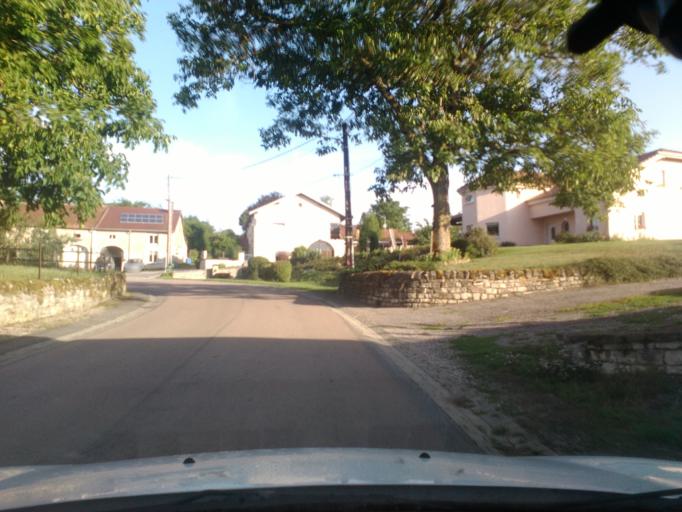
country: FR
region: Lorraine
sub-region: Departement des Vosges
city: Mirecourt
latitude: 48.2800
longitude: 6.0435
